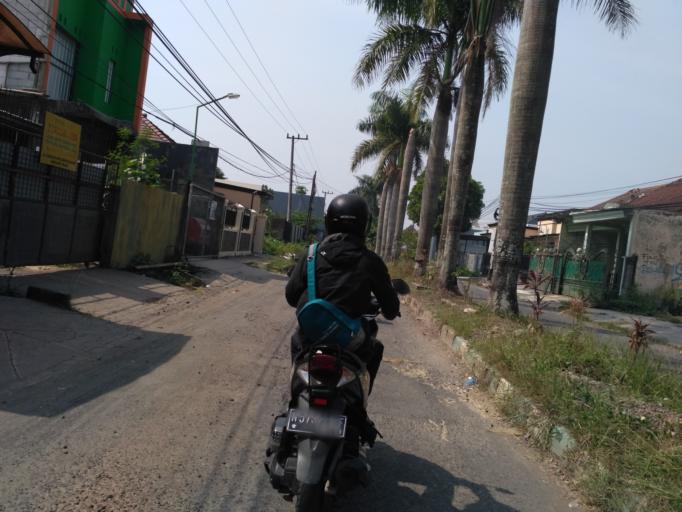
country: ID
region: East Java
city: Malang
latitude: -7.9663
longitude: 112.6686
